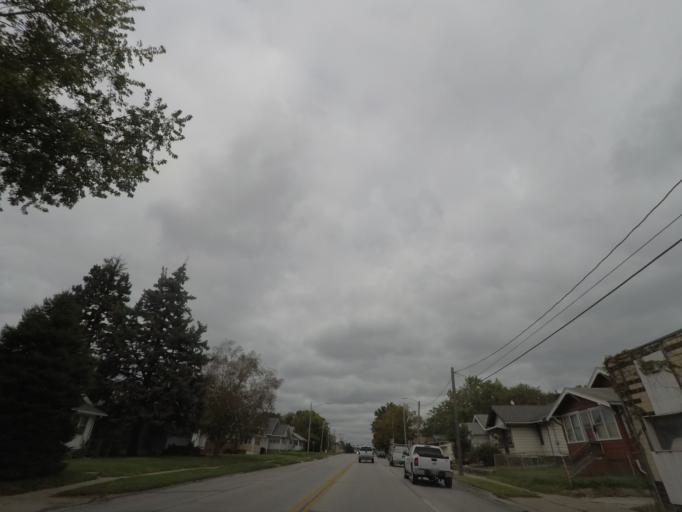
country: US
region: Iowa
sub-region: Polk County
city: Des Moines
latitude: 41.6167
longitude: -93.6006
